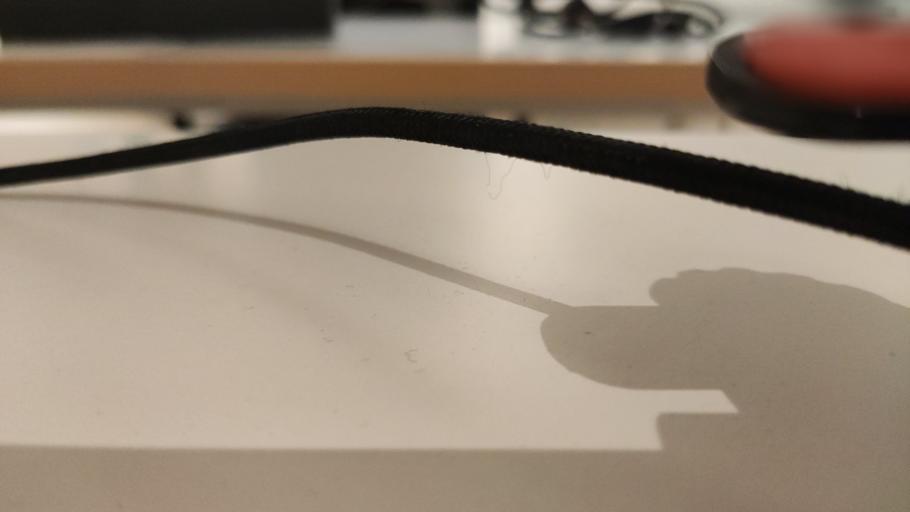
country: RU
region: Moskovskaya
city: Dorokhovo
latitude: 55.4326
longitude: 36.3520
